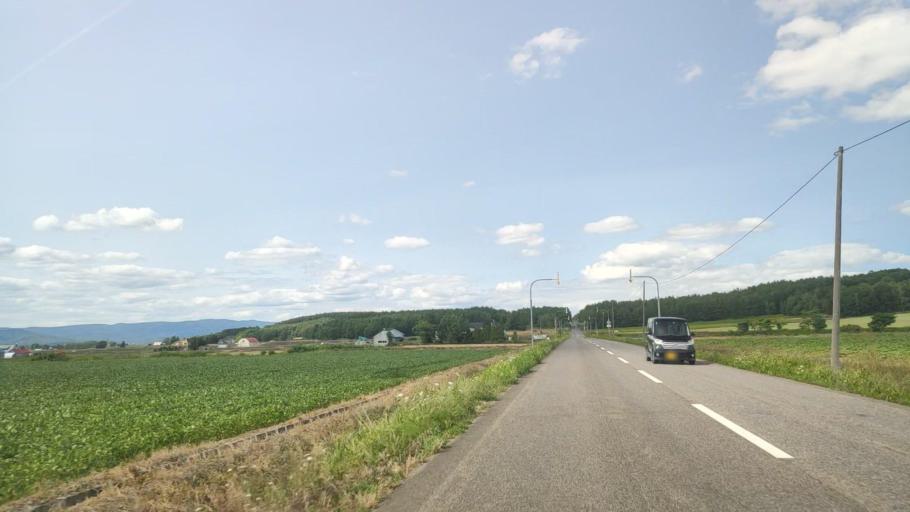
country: JP
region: Hokkaido
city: Nayoro
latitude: 44.2373
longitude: 142.4157
